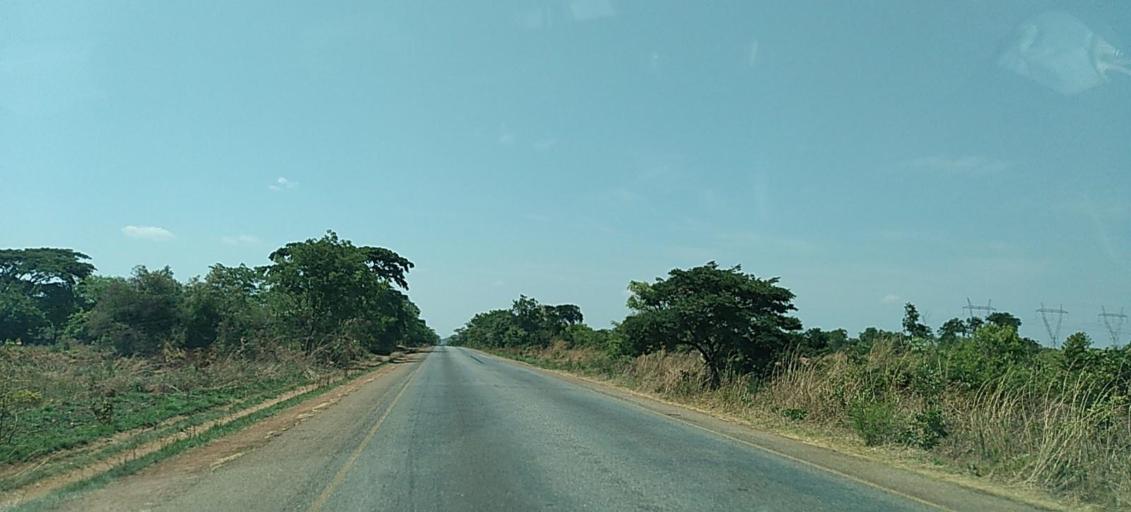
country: ZM
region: Central
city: Kapiri Mposhi
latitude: -13.6770
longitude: 28.6280
